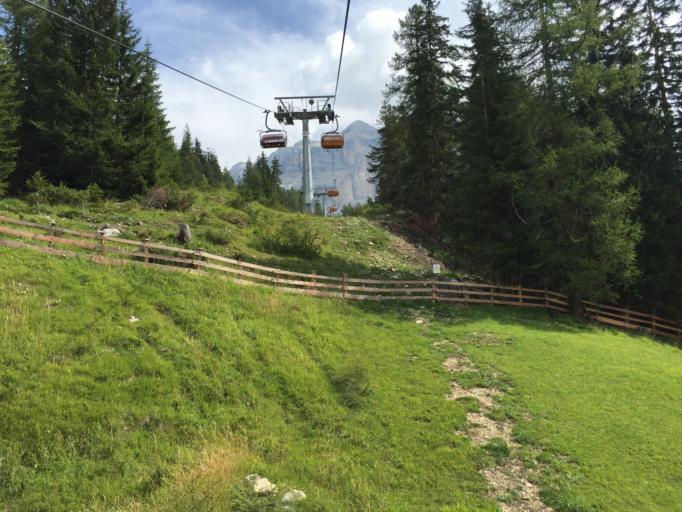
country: IT
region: Trentino-Alto Adige
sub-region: Bolzano
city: Badia
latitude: 46.6114
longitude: 11.9144
